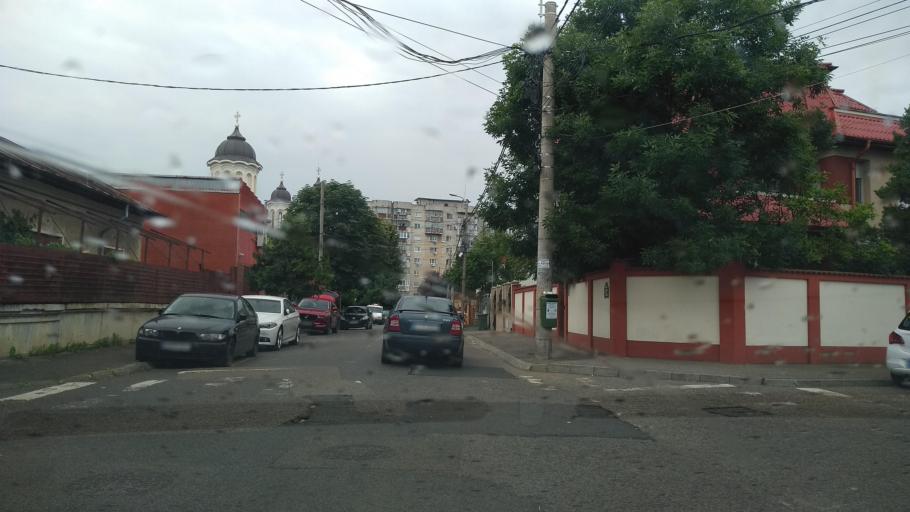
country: RO
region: Ilfov
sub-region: Comuna Fundeni-Dobroesti
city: Fundeni
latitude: 44.4574
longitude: 26.1418
